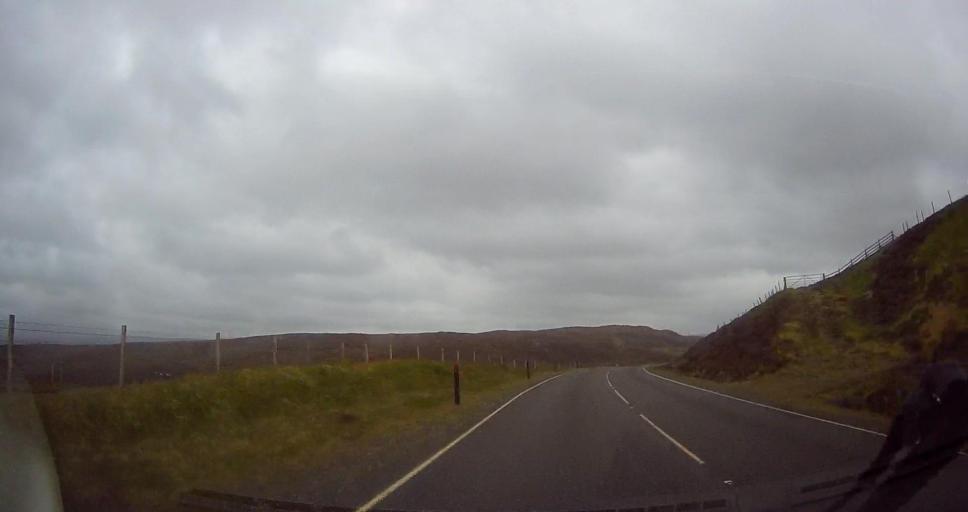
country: GB
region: Scotland
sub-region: Shetland Islands
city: Lerwick
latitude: 60.4514
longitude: -1.3958
